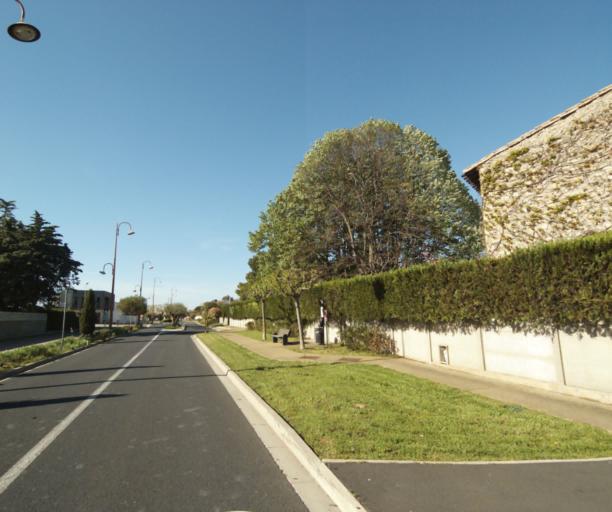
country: FR
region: Languedoc-Roussillon
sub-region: Departement de l'Herault
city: Perols
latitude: 43.5648
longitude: 3.9498
